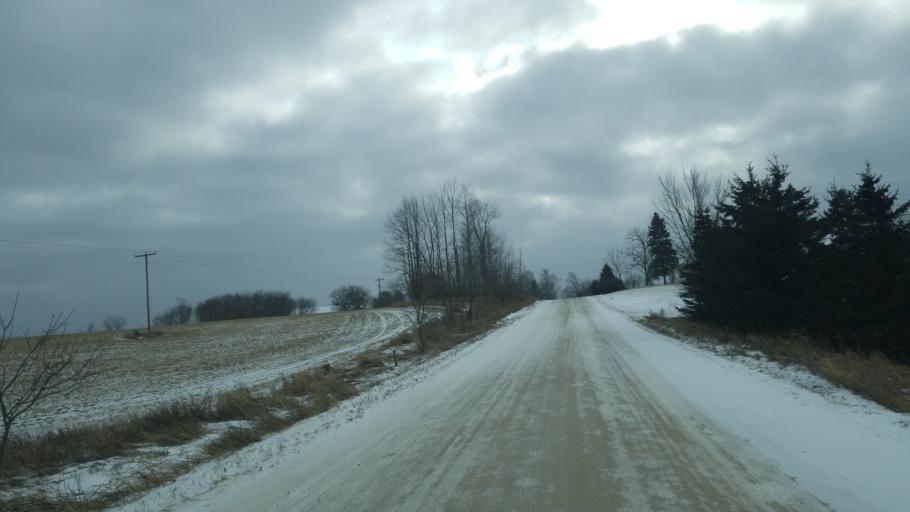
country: US
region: Michigan
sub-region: Osceola County
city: Evart
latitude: 44.0268
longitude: -85.2269
